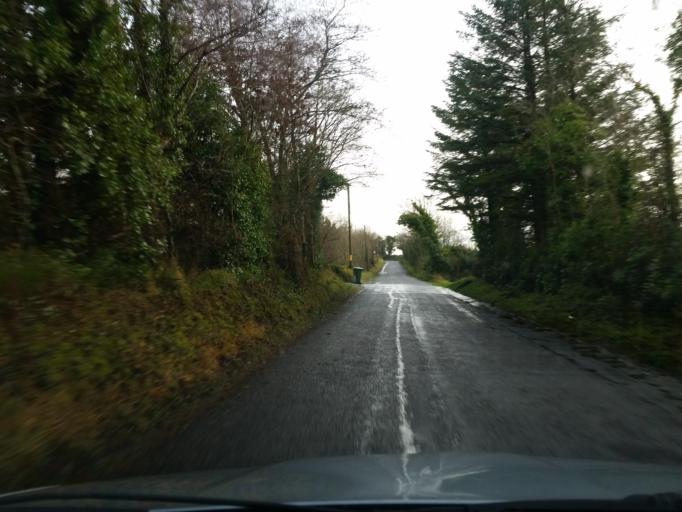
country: GB
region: Northern Ireland
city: Lisnaskea
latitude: 54.2738
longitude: -7.3991
